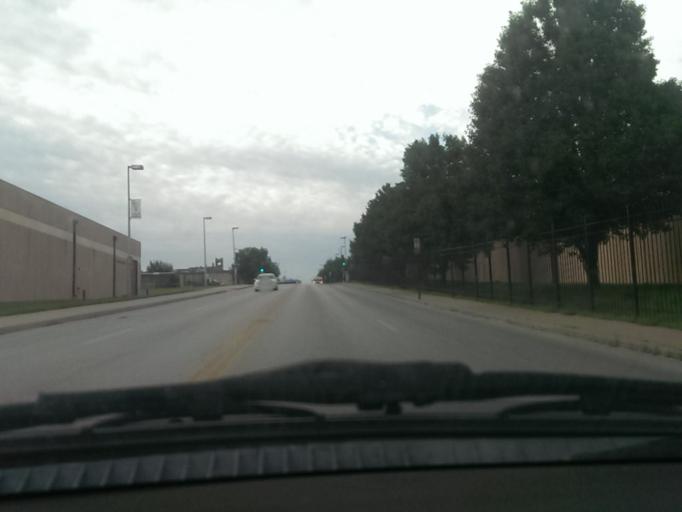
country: US
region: Missouri
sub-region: Jackson County
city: Kansas City
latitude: 39.0983
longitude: -94.5700
